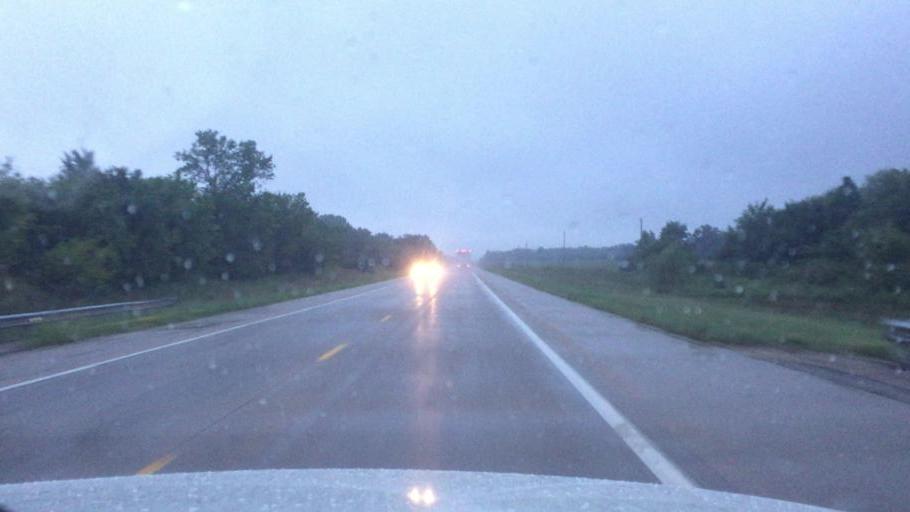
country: US
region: Kansas
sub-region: Neosho County
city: Chanute
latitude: 37.5568
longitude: -95.4709
